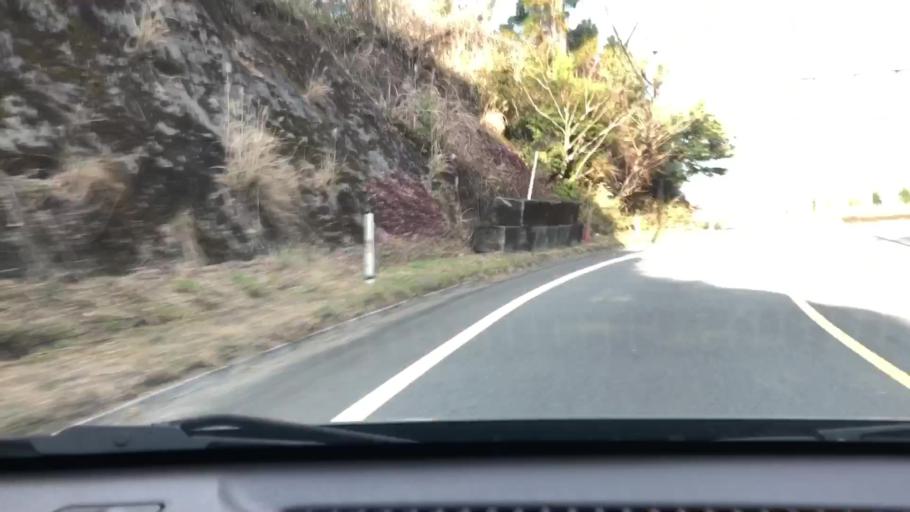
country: JP
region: Miyazaki
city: Miyazaki-shi
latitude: 31.8203
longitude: 131.2963
